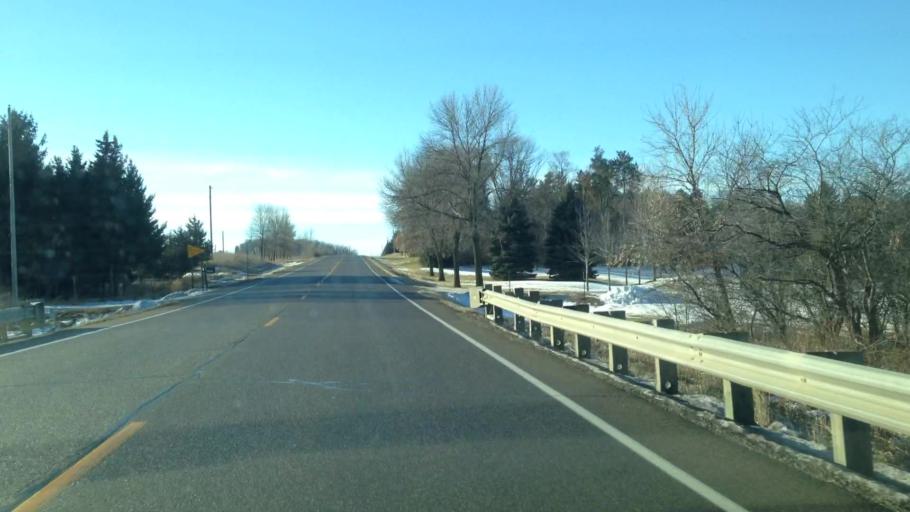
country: US
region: Minnesota
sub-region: Goodhue County
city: Cannon Falls
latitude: 44.6007
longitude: -93.0091
